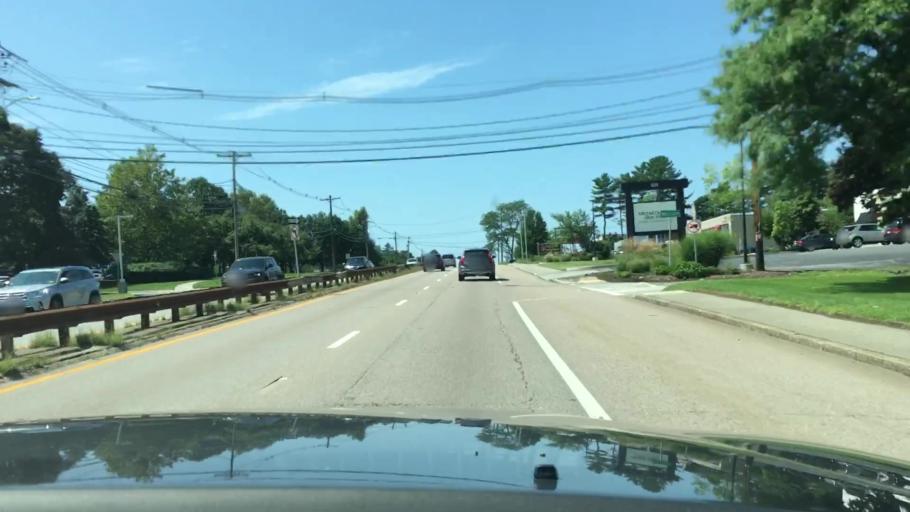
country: US
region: Massachusetts
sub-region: Middlesex County
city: Natick
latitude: 42.3013
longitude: -71.3488
